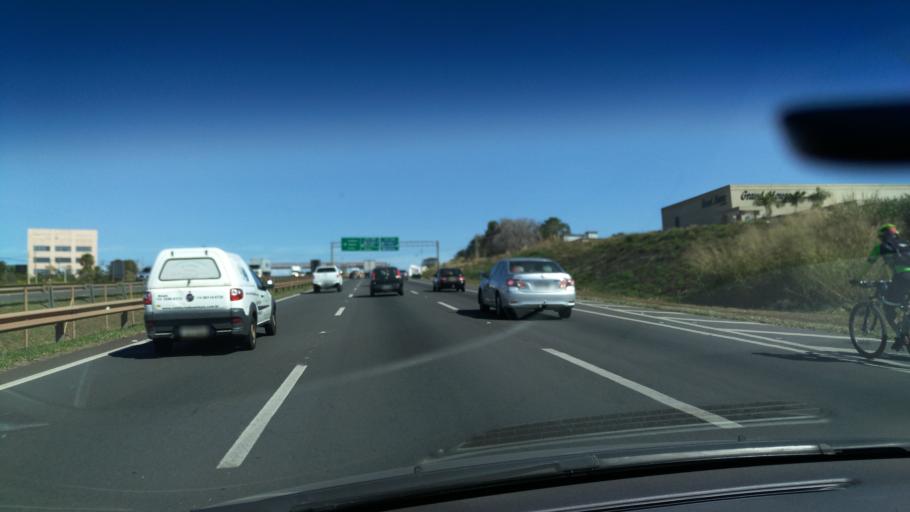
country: BR
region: Sao Paulo
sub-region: Campinas
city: Campinas
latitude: -22.8371
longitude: -47.0348
